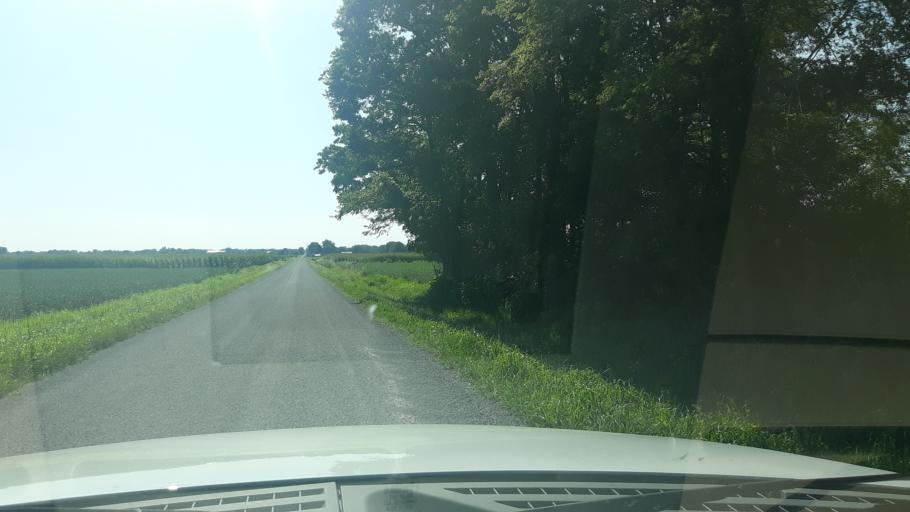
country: US
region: Illinois
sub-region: Saline County
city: Eldorado
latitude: 37.8633
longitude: -88.4925
